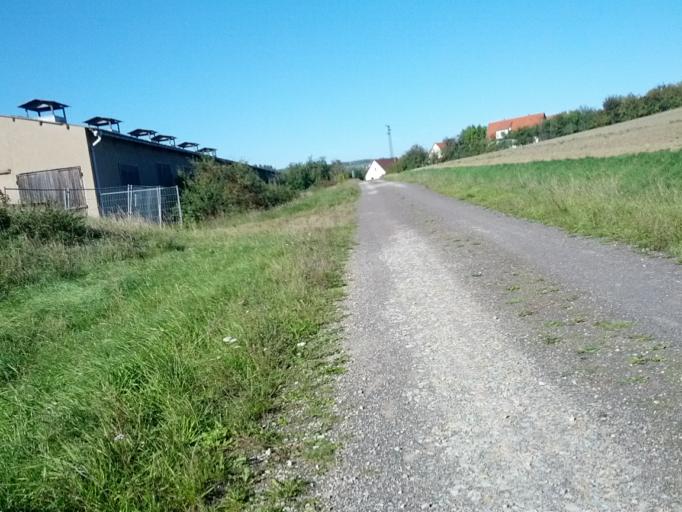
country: DE
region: Thuringia
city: Krauthausen
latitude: 51.0130
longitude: 10.2894
